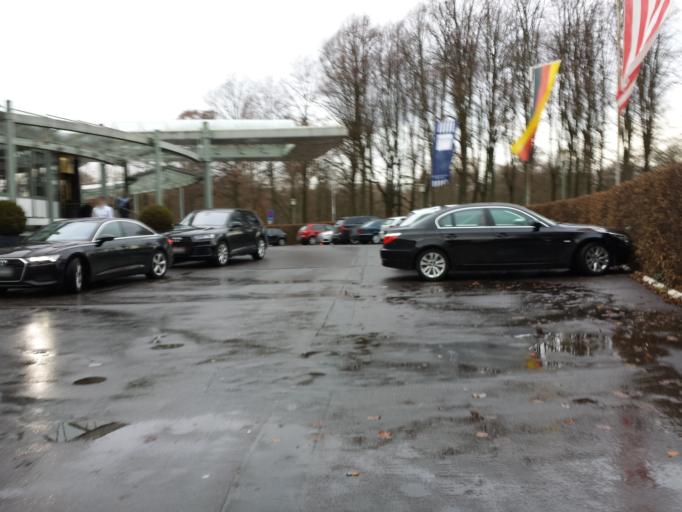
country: DE
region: Bremen
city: Bremen
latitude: 53.0891
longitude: 8.8224
